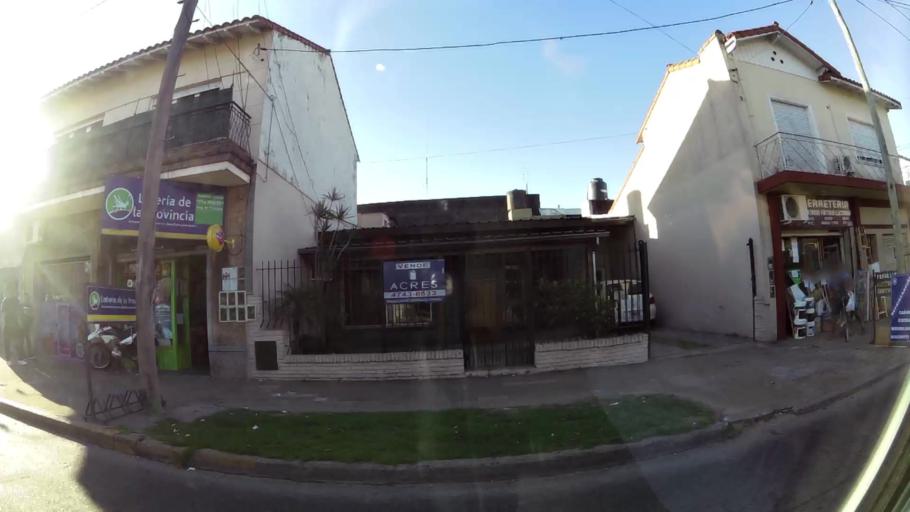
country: AR
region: Buenos Aires
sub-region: Partido de San Isidro
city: San Isidro
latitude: -34.4707
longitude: -58.5472
